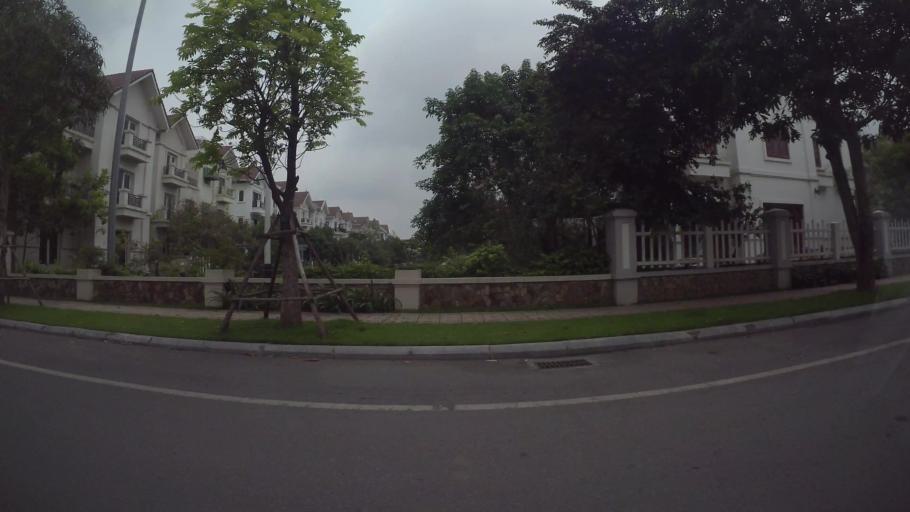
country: VN
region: Ha Noi
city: Trau Quy
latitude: 21.0418
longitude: 105.9166
